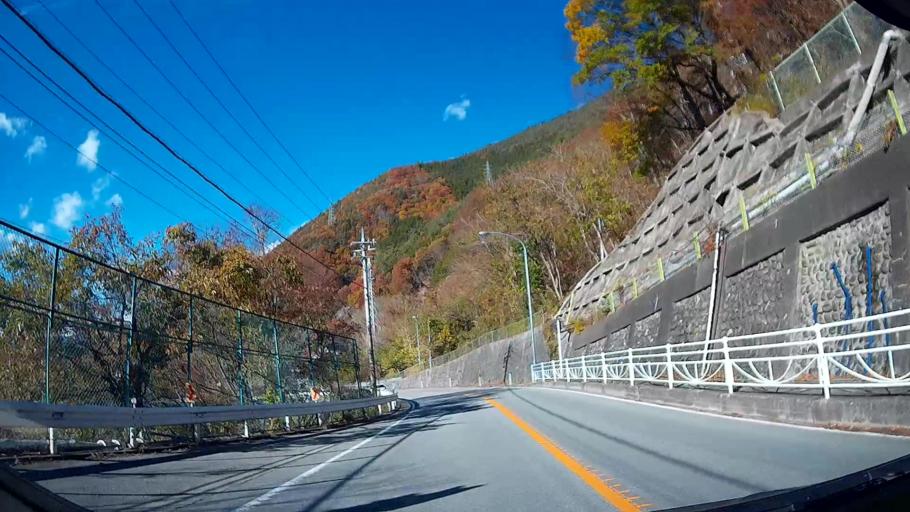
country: JP
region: Yamanashi
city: Enzan
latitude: 35.6456
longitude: 138.7655
